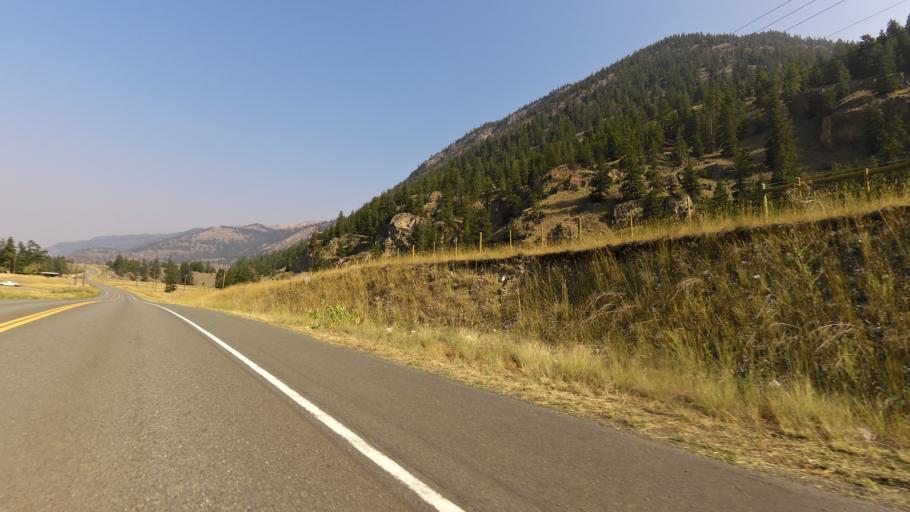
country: CA
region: British Columbia
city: Princeton
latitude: 49.3401
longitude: -120.0585
